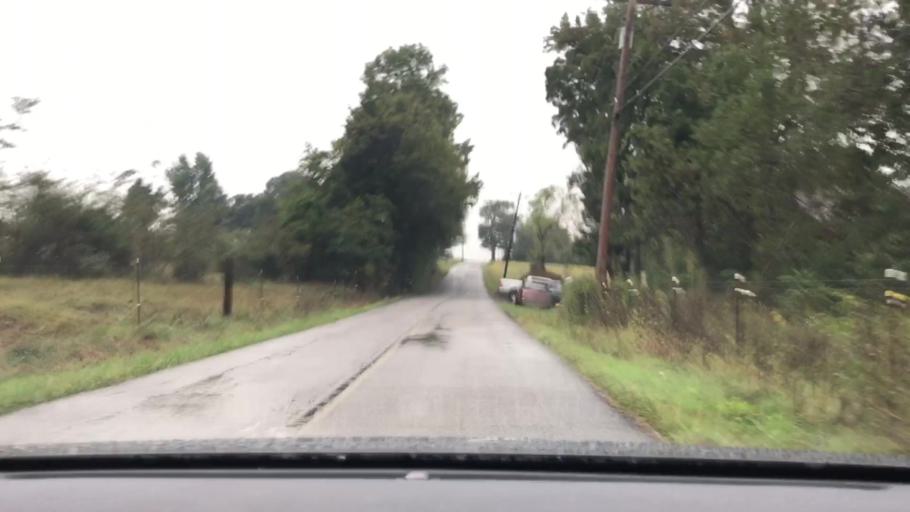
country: US
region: Tennessee
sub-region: Sumner County
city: Portland
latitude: 36.5309
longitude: -86.4971
